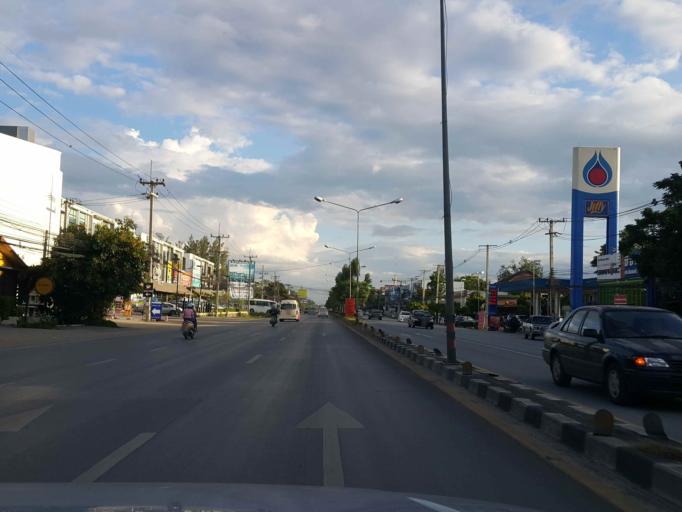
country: TH
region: Chiang Mai
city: San Sai
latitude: 18.8299
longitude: 99.0125
